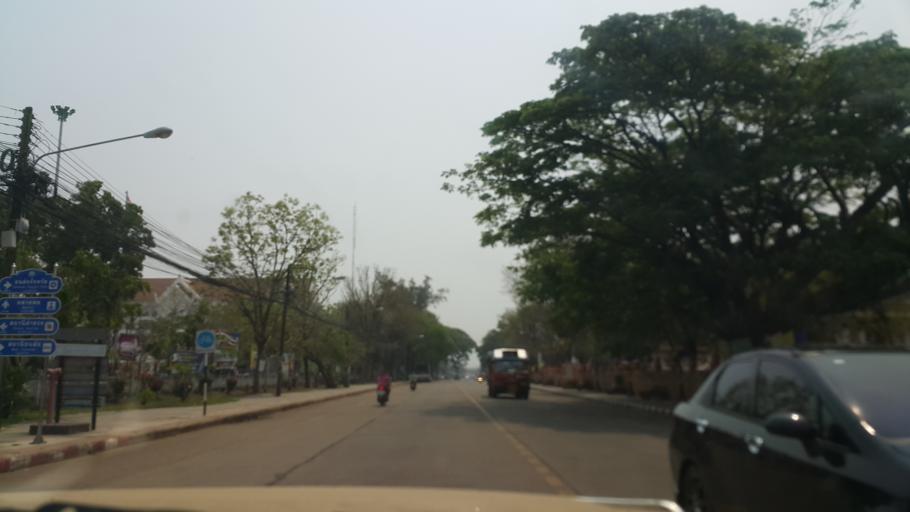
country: TH
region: Nakhon Phanom
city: Nakhon Phanom
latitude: 17.4088
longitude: 104.7806
